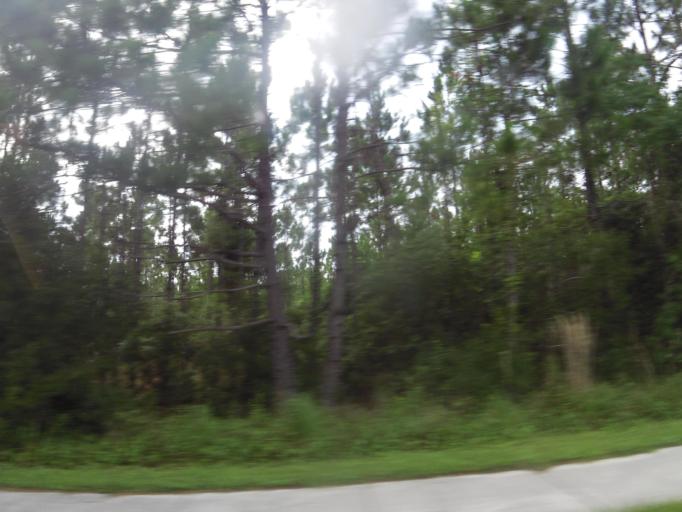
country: US
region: Florida
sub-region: Duval County
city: Jacksonville Beach
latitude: 30.2623
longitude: -81.4517
